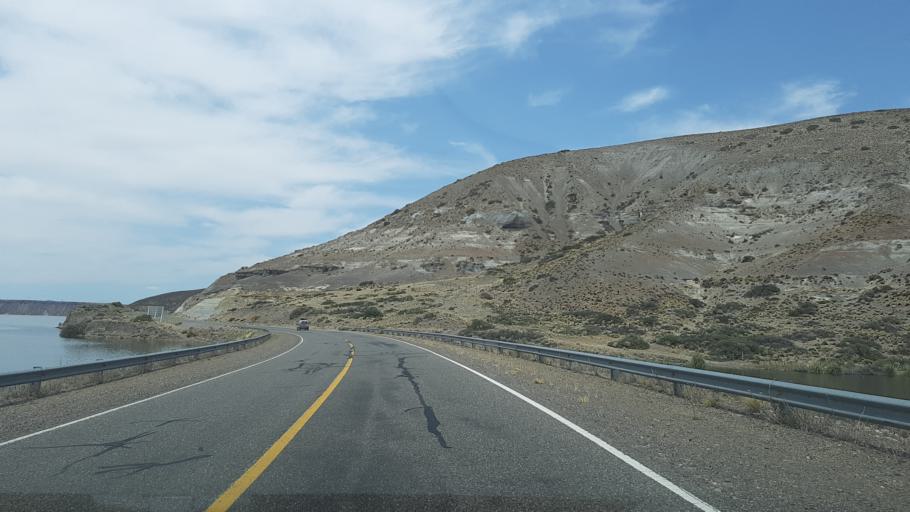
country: AR
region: Neuquen
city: Junin de los Andes
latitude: -40.4579
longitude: -70.6639
